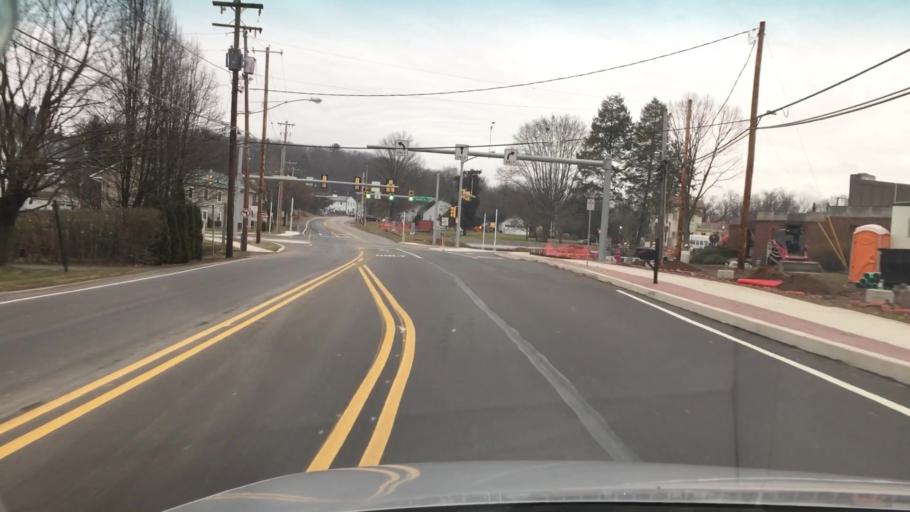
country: US
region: Pennsylvania
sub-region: Columbia County
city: Bloomsburg
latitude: 41.0112
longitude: -76.4446
